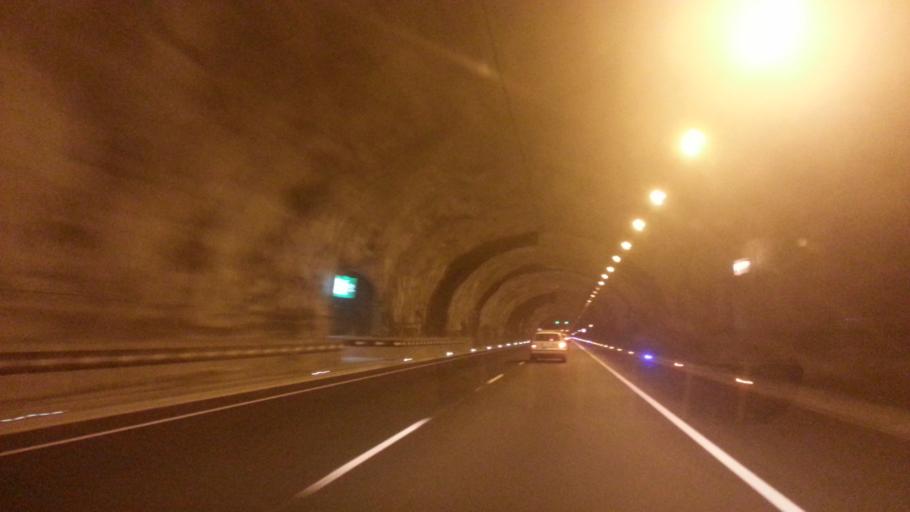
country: ES
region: Catalonia
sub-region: Provincia de Barcelona
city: Sant Pere de Ribes
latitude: 41.2638
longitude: 1.7331
